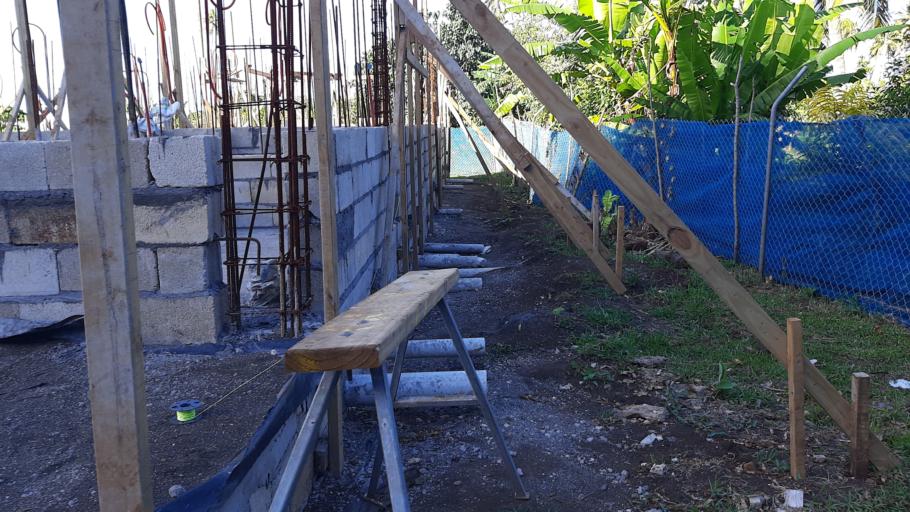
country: VU
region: Tafea
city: Isangel
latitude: -18.7461
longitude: 169.2032
